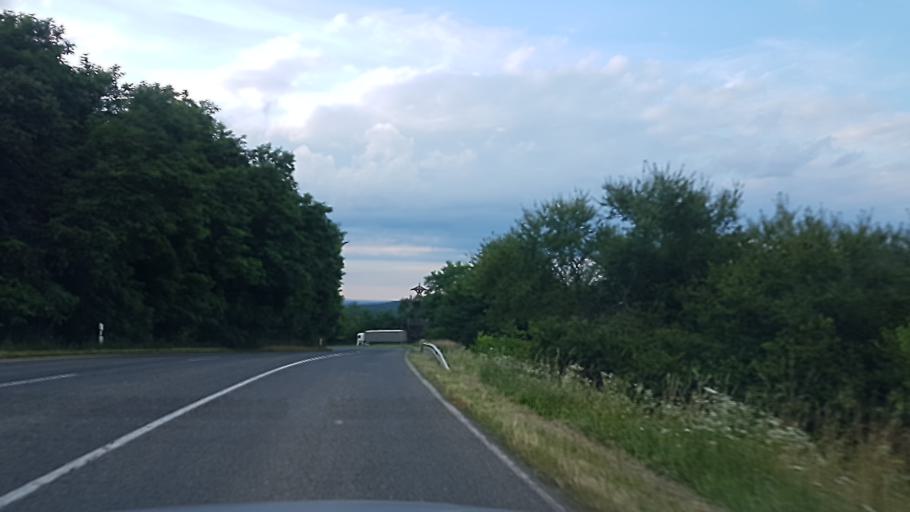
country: HU
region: Somogy
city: Kaposvar
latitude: 46.2692
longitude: 17.8251
